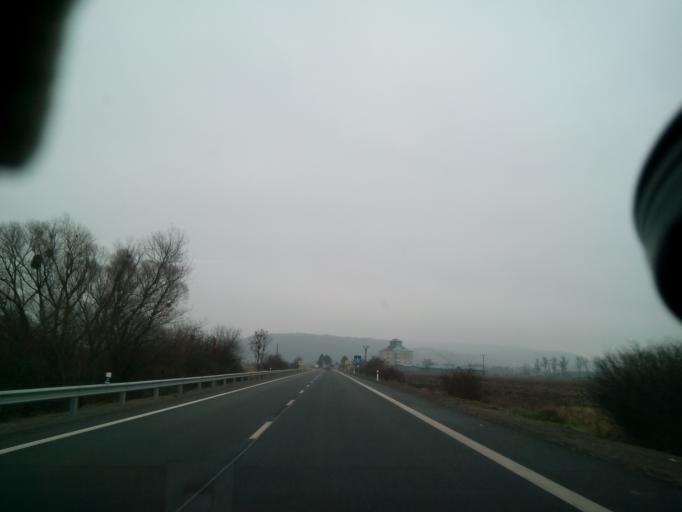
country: SK
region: Kosicky
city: Kosice
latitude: 48.7333
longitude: 21.4349
